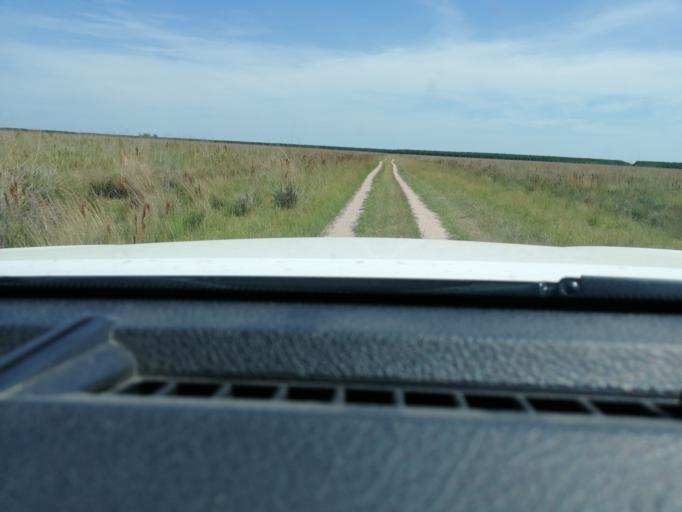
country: AR
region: Corrientes
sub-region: Departamento de San Miguel
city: San Miguel
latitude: -28.0526
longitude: -57.4553
